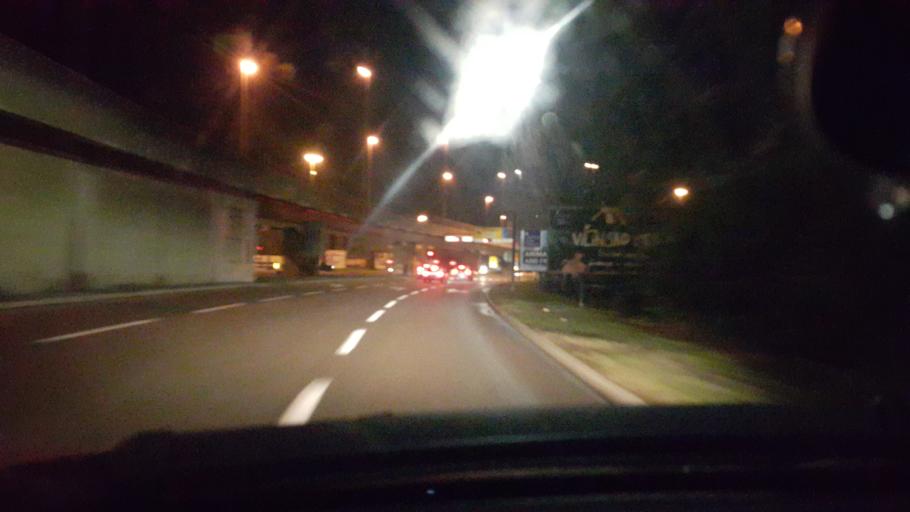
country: SI
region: Maribor
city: Maribor
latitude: 46.5596
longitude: 15.6609
